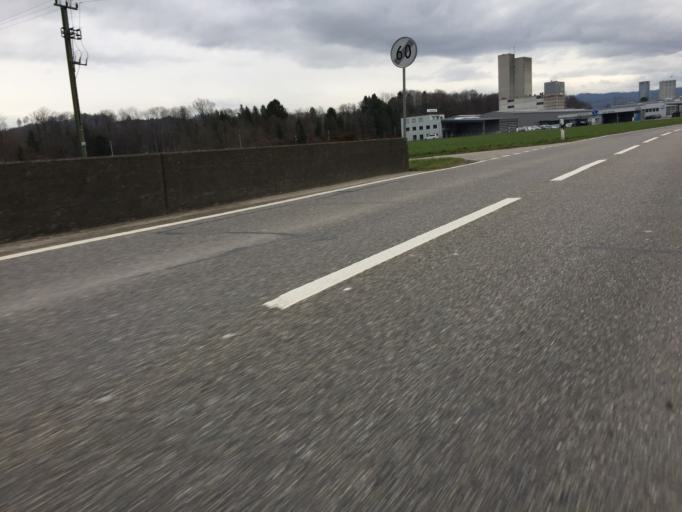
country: CH
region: Bern
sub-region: Emmental District
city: Kirchberg
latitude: 47.0752
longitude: 7.5862
